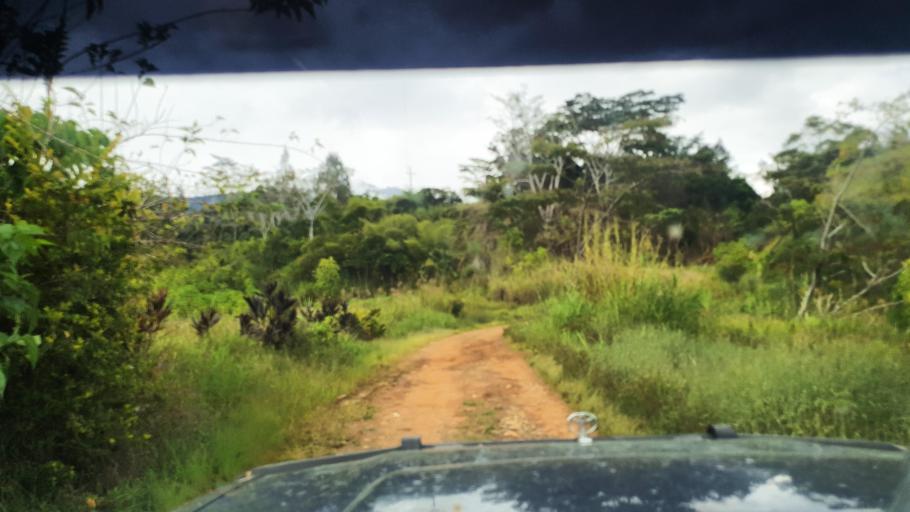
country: PG
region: Jiwaka
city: Minj
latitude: -5.8912
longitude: 144.8174
